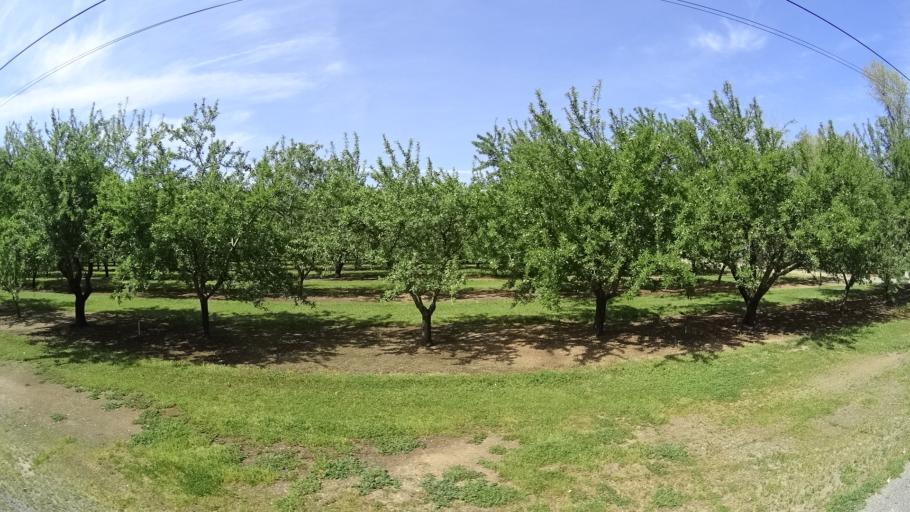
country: US
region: California
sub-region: Glenn County
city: Hamilton City
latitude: 39.8014
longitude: -122.0570
